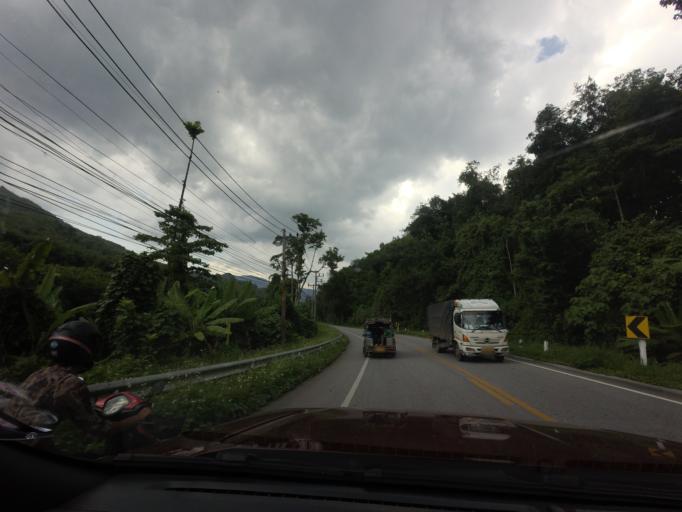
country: TH
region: Yala
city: Than To
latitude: 6.2251
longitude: 101.1655
